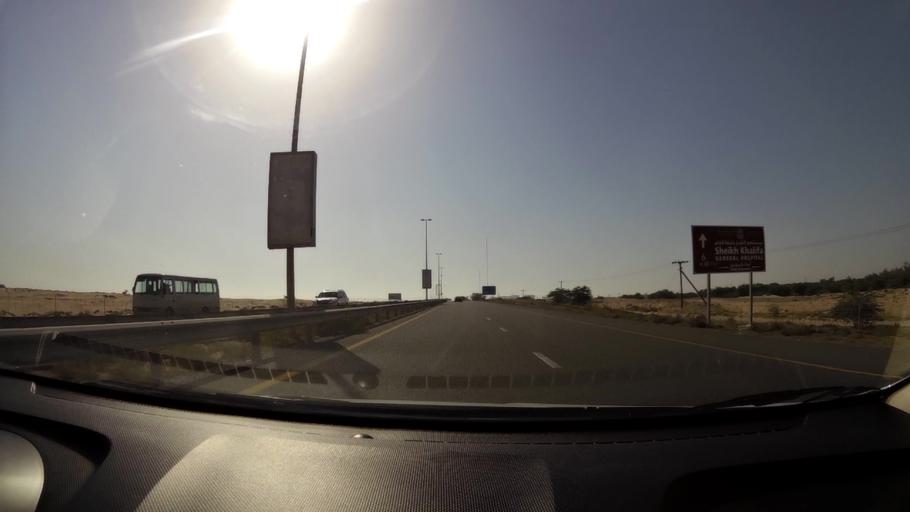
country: AE
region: Umm al Qaywayn
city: Umm al Qaywayn
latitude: 25.4752
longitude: 55.5732
